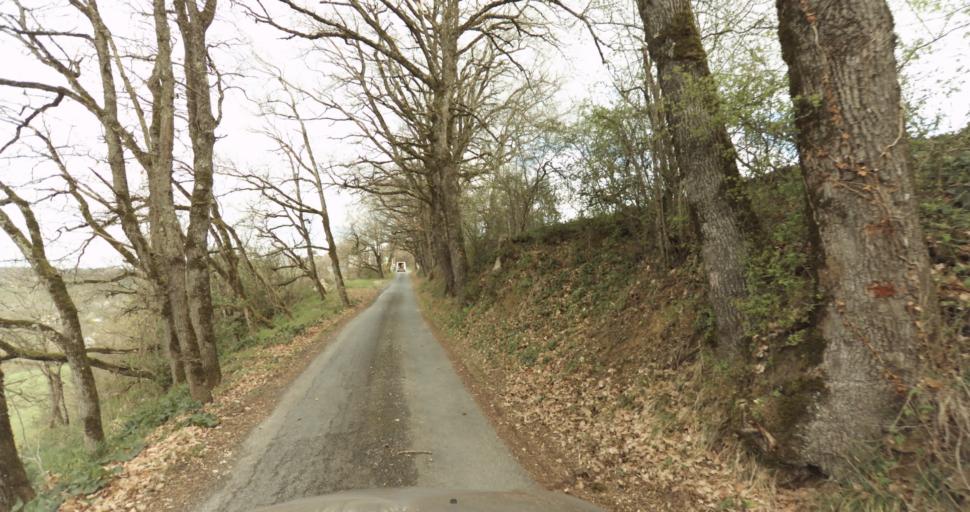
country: FR
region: Midi-Pyrenees
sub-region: Departement du Tarn
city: Puygouzon
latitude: 43.8687
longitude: 2.1908
